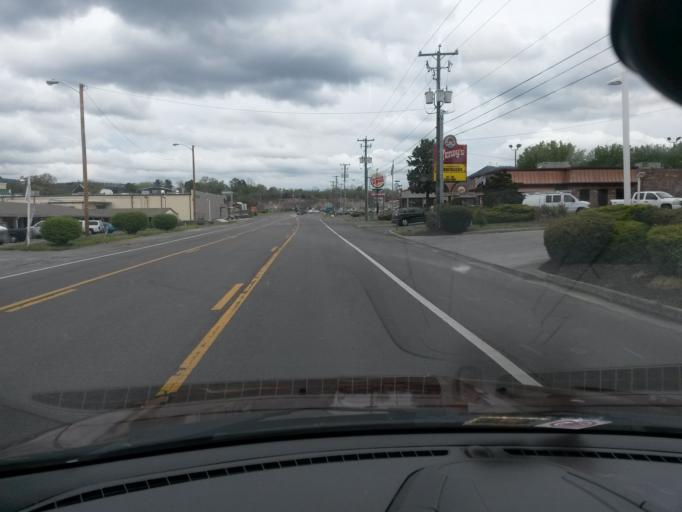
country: US
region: Virginia
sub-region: Roanoke County
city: Hollins
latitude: 37.3438
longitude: -79.9559
